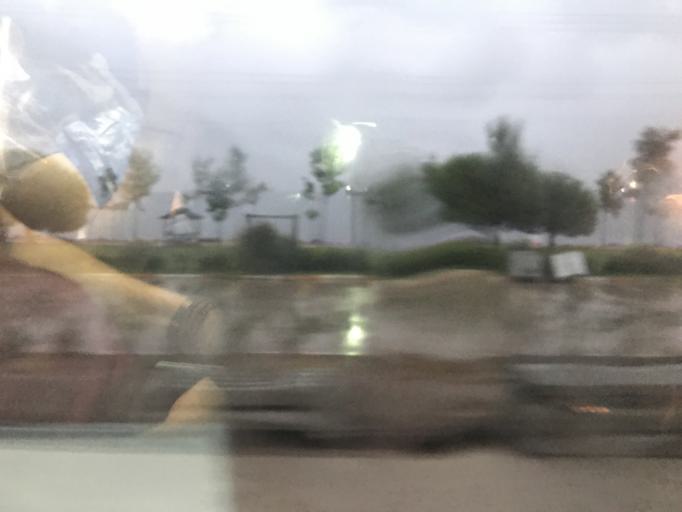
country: TR
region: Kocaeli
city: Hereke
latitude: 40.7761
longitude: 29.6359
